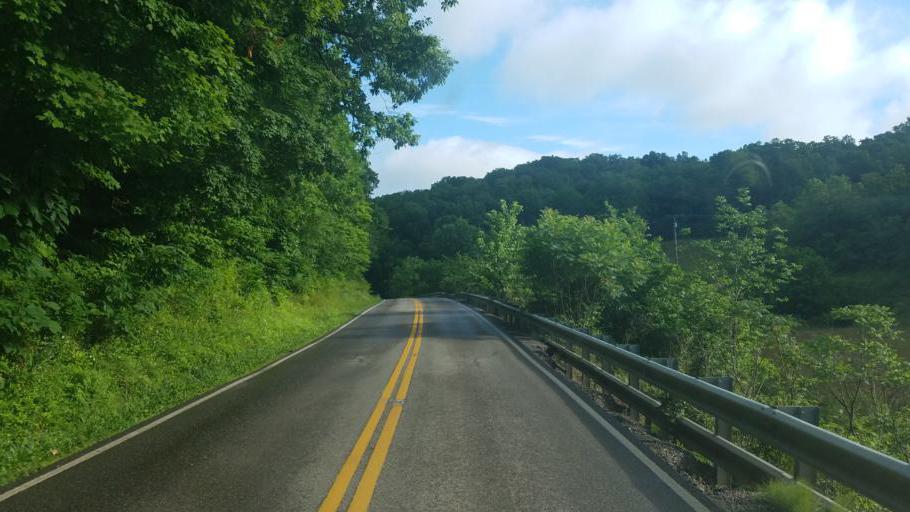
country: US
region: Ohio
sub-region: Gallia County
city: Gallipolis
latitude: 38.7702
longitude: -82.3550
